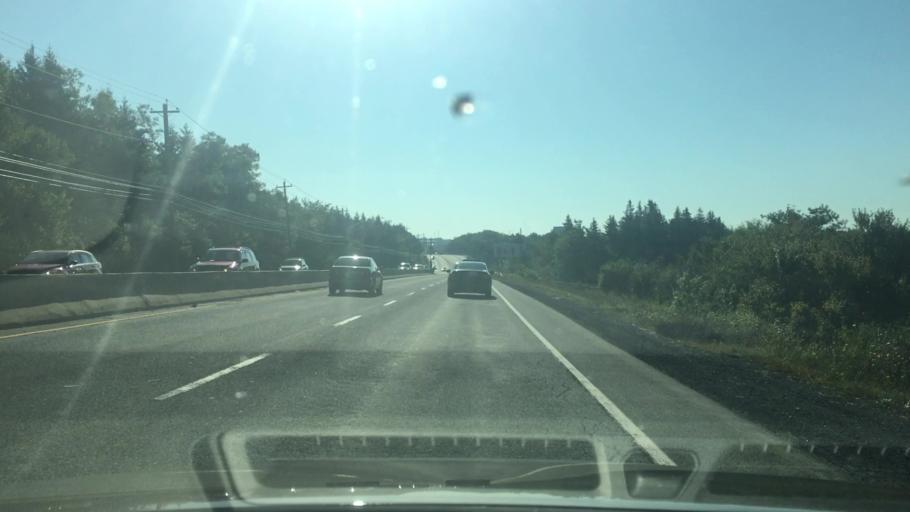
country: CA
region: Nova Scotia
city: Dartmouth
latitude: 44.7073
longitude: -63.6213
